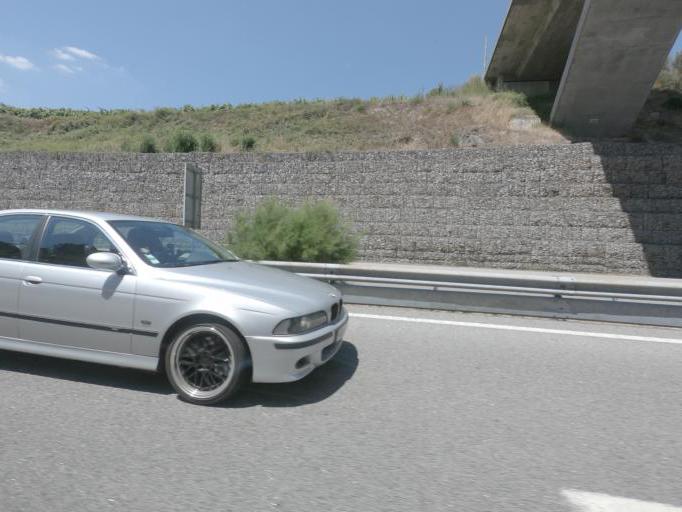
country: PT
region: Porto
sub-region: Marco de Canaveses
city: Marco de Canavezes
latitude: 41.2248
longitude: -8.1443
